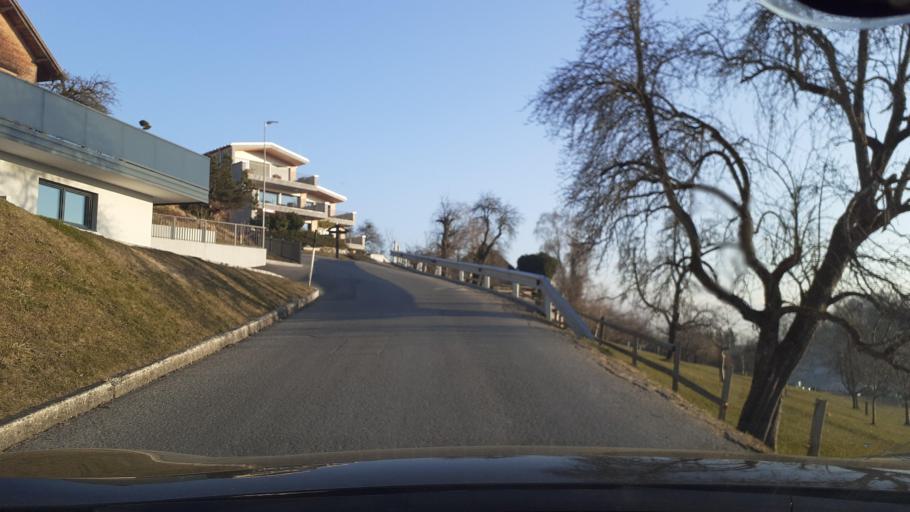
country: AT
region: Vorarlberg
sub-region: Politischer Bezirk Feldkirch
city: Fraxern
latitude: 47.3155
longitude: 9.6721
